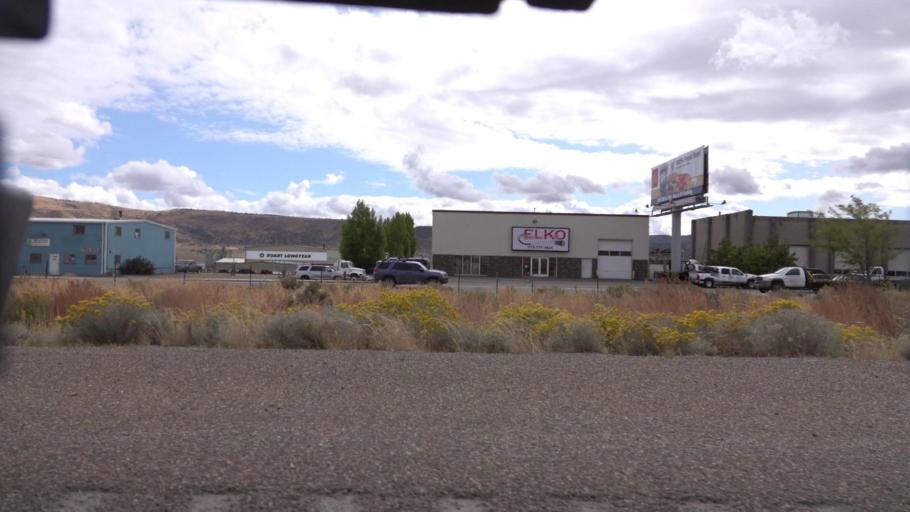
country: US
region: Nevada
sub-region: Elko County
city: Elko
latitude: 40.8680
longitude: -115.7302
